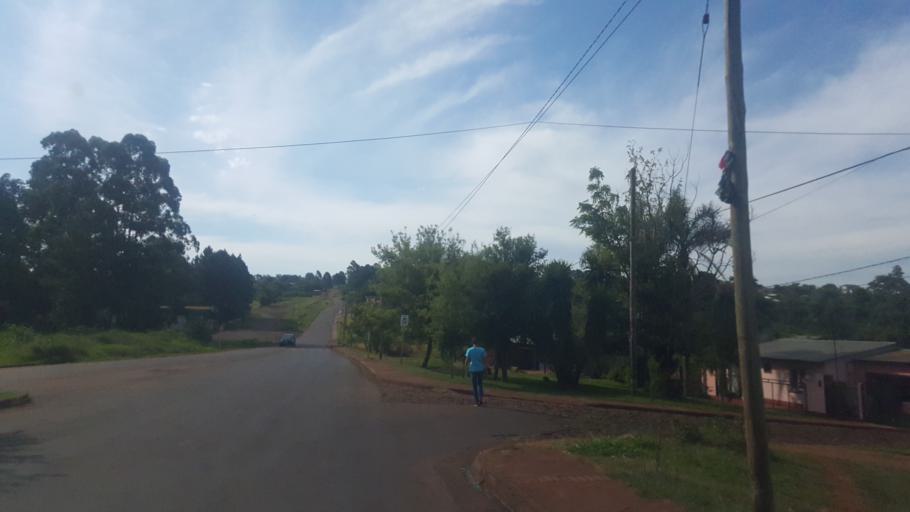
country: AR
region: Misiones
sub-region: Departamento de Leandro N. Alem
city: Leandro N. Alem
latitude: -27.5969
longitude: -55.3337
